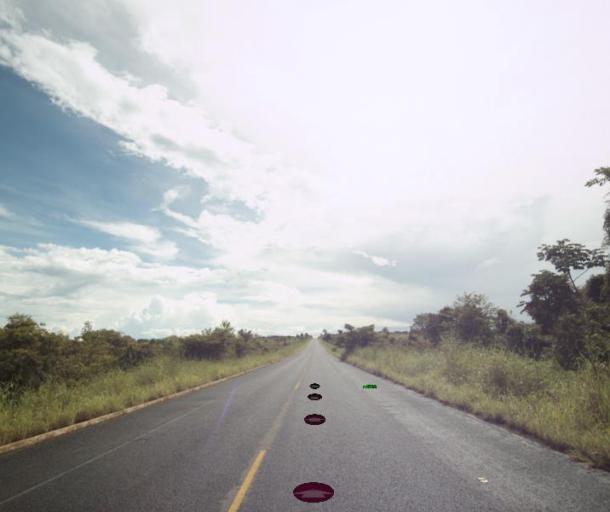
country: BR
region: Goias
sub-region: Sao Miguel Do Araguaia
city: Sao Miguel do Araguaia
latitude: -13.3013
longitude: -50.2897
